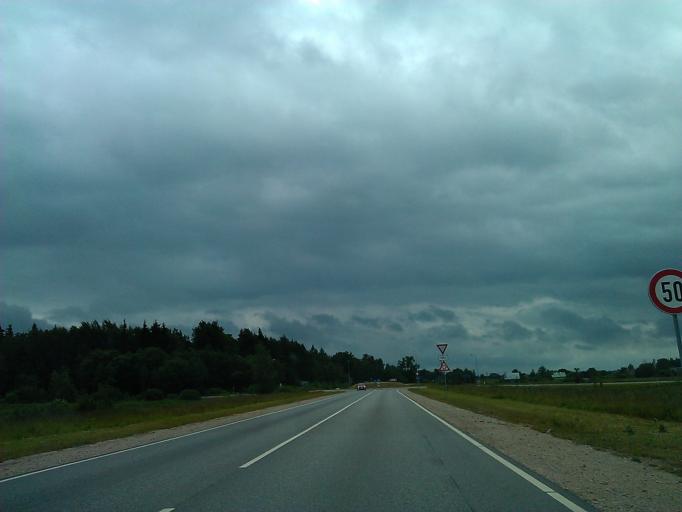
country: LV
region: Kuldigas Rajons
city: Kuldiga
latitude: 56.9736
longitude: 22.0156
